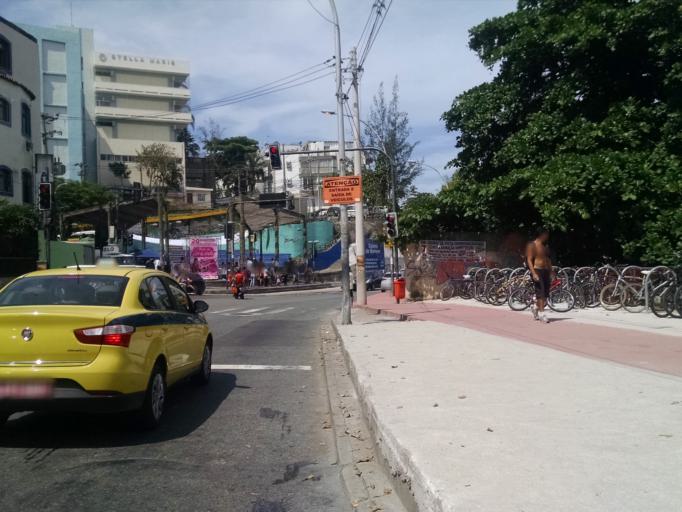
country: BR
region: Rio de Janeiro
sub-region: Rio De Janeiro
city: Rio de Janeiro
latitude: -22.9951
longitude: -43.2349
